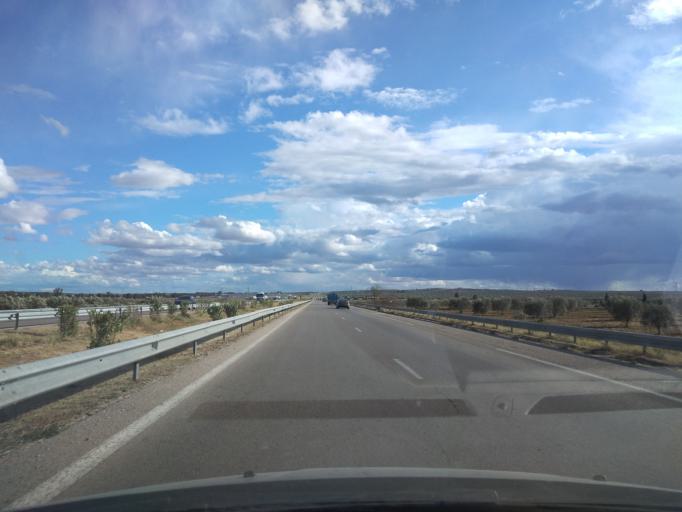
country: TN
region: Al Munastir
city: Manzil Kamil
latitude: 35.5769
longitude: 10.6100
